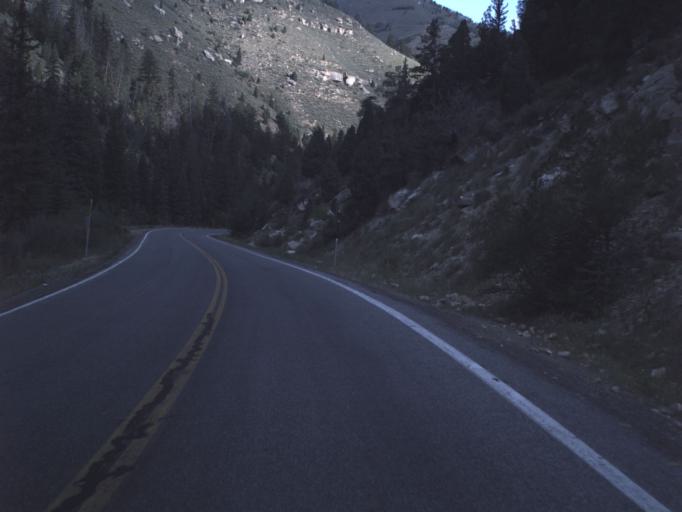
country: US
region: Utah
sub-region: Emery County
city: Huntington
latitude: 39.4751
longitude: -111.1566
